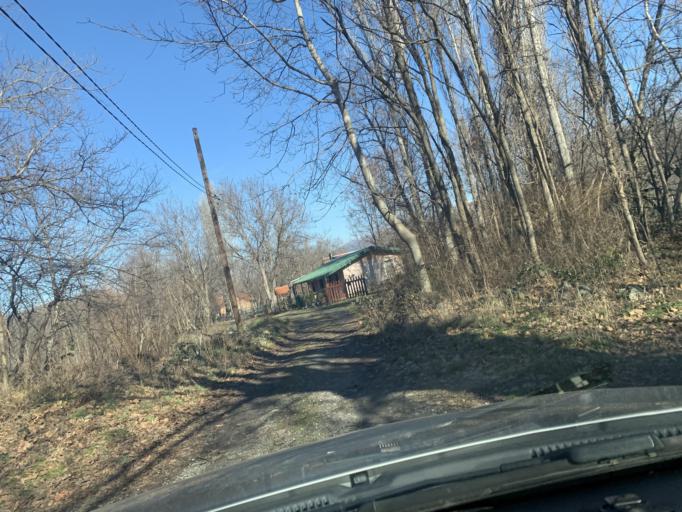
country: MK
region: Demir Kapija
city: Demir Kapija
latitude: 41.3886
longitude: 22.2219
